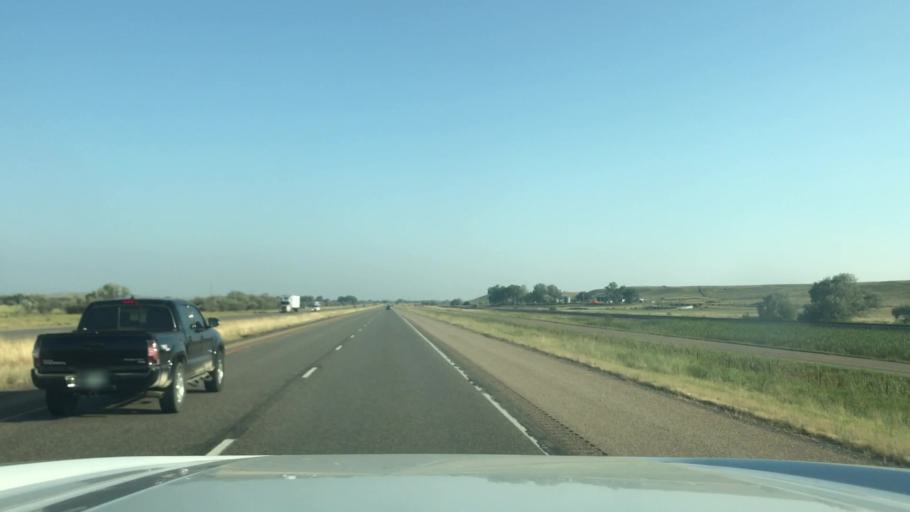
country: US
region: Montana
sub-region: Big Horn County
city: Crow Agency
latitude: 45.6436
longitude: -107.4729
